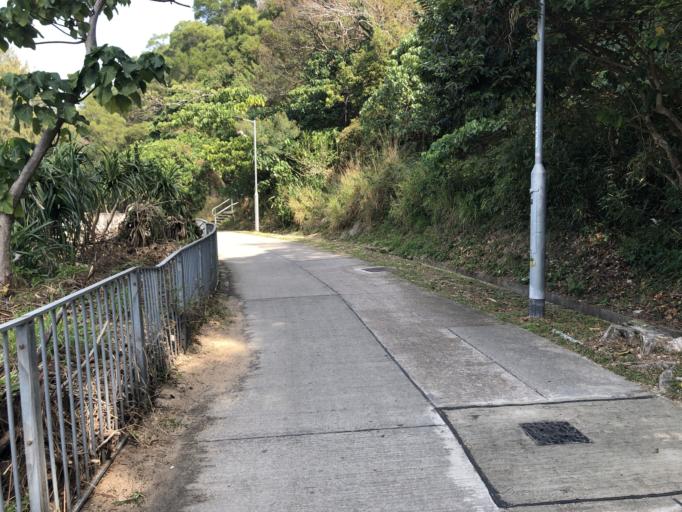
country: HK
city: Yung Shue Wan
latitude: 22.2144
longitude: 114.0252
